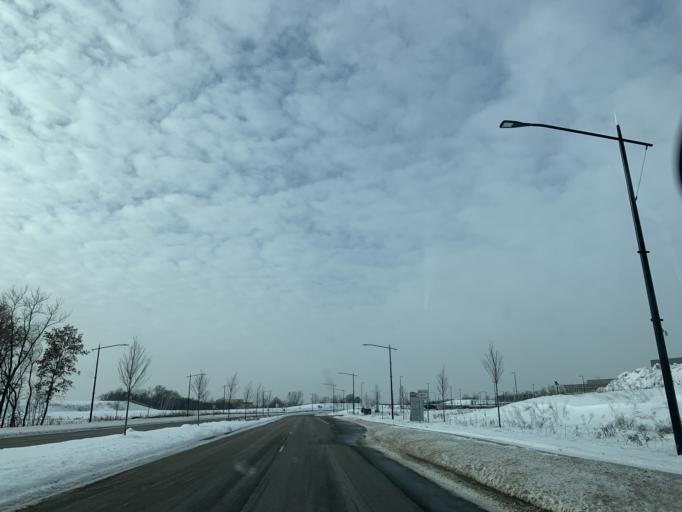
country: US
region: Minnesota
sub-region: Dakota County
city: Mendota Heights
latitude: 44.8567
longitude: -93.1135
